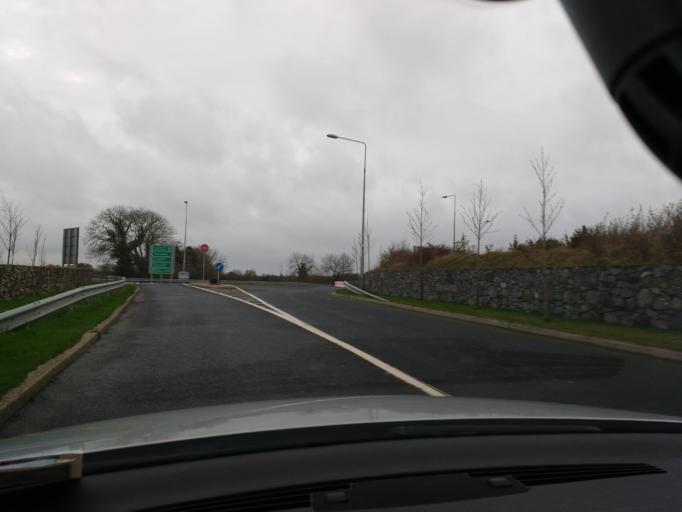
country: IE
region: Munster
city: Thurles
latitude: 52.6719
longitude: -7.7174
